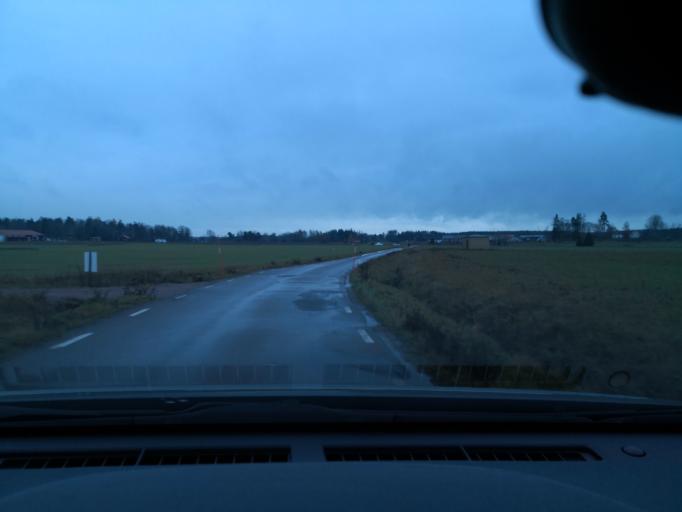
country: SE
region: Vaestmanland
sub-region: Hallstahammars Kommun
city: Kolback
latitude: 59.5638
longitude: 16.2012
